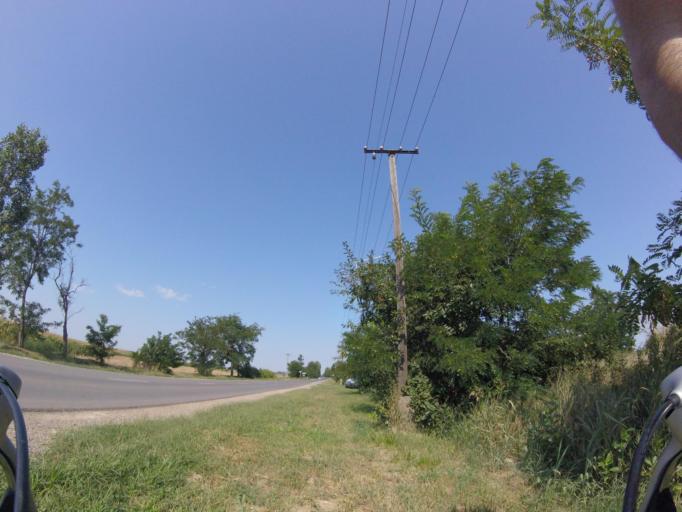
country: HU
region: Bacs-Kiskun
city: Bacsbokod
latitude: 46.1274
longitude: 19.1440
